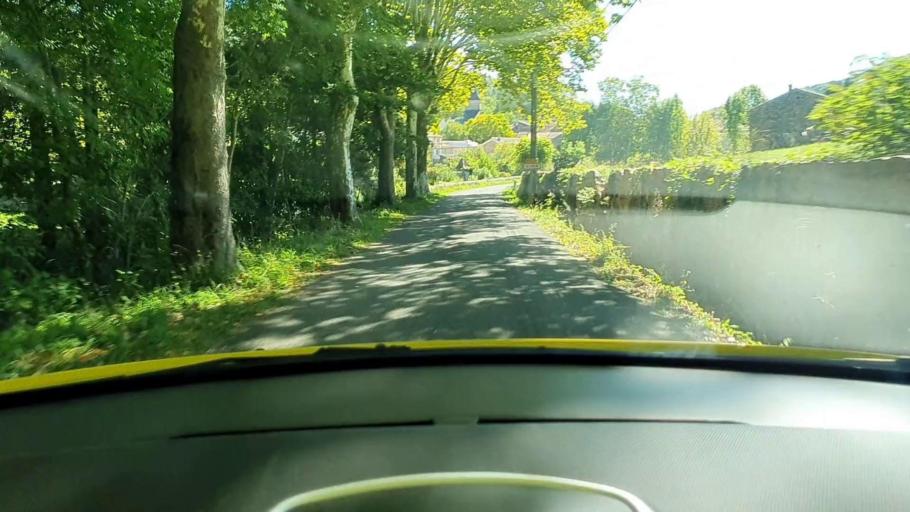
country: FR
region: Languedoc-Roussillon
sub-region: Departement du Gard
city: Le Vigan
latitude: 43.9693
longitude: 3.4382
